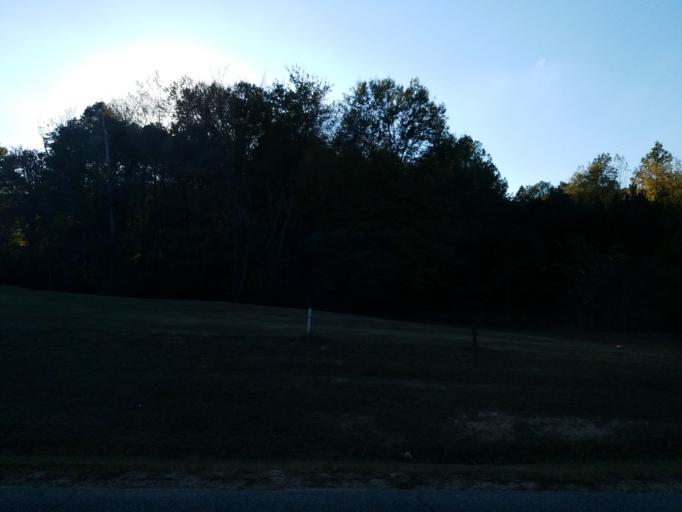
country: US
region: Georgia
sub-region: Bartow County
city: Euharlee
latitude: 34.2197
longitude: -84.9359
